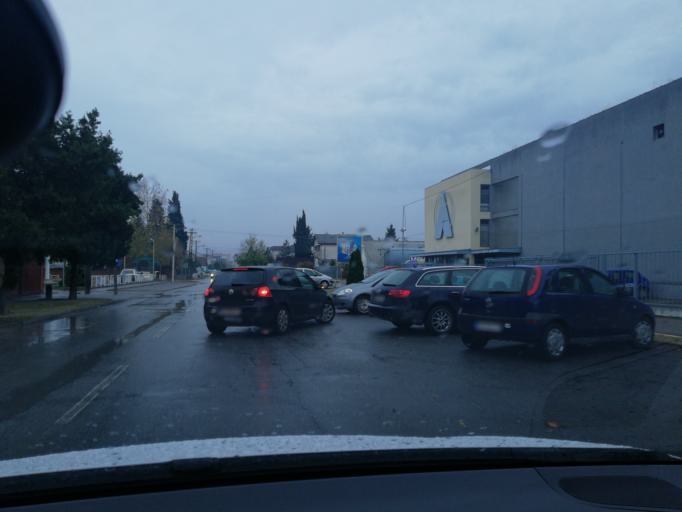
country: RS
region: Autonomna Pokrajina Vojvodina
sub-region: Juznobacki Okrug
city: Novi Sad
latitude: 45.2458
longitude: 19.8007
